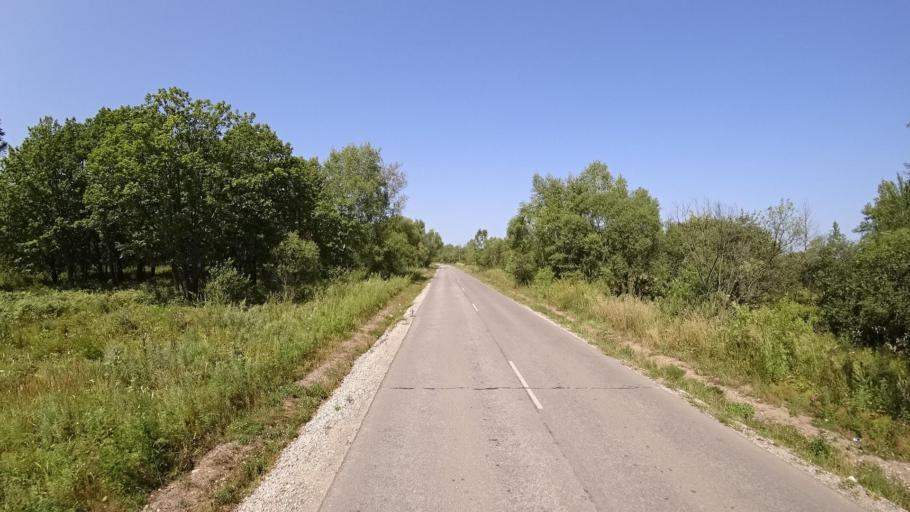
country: RU
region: Khabarovsk Krai
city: Khor
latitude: 47.9743
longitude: 135.1137
